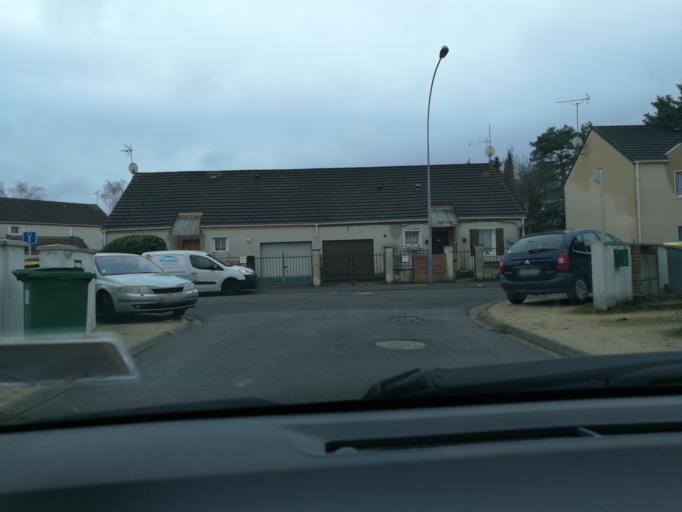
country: FR
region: Centre
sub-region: Departement du Loiret
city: Fleury-les-Aubrais
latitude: 47.9392
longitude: 1.9287
